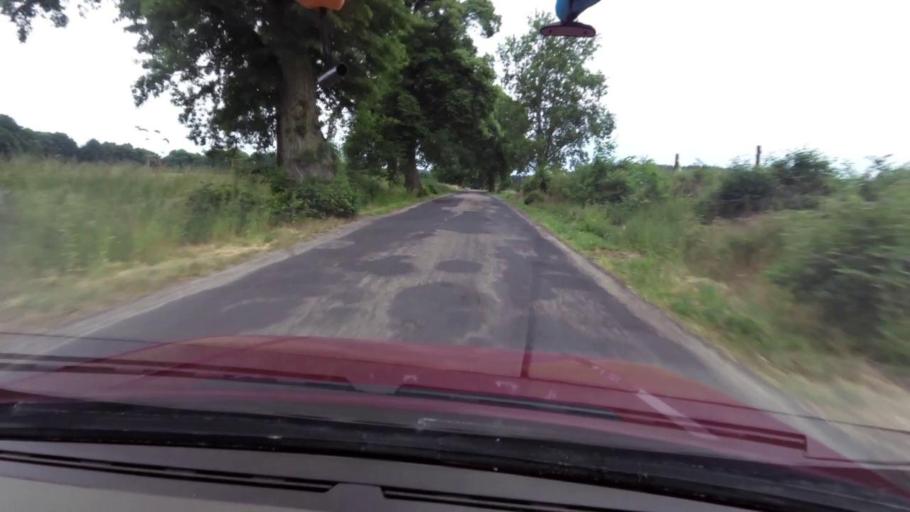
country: PL
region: Pomeranian Voivodeship
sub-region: Powiat slupski
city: Kepice
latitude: 54.2182
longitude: 16.8393
